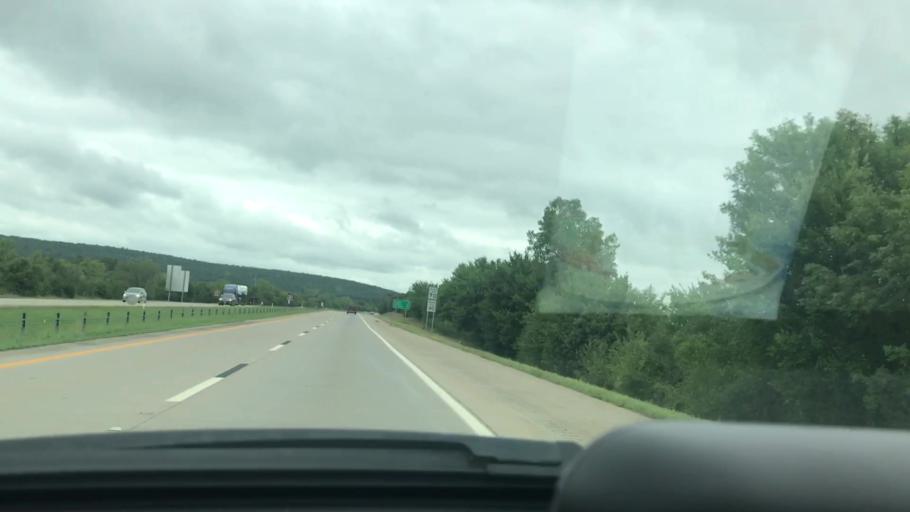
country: US
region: Oklahoma
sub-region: Pittsburg County
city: Krebs
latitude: 35.0087
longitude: -95.7187
